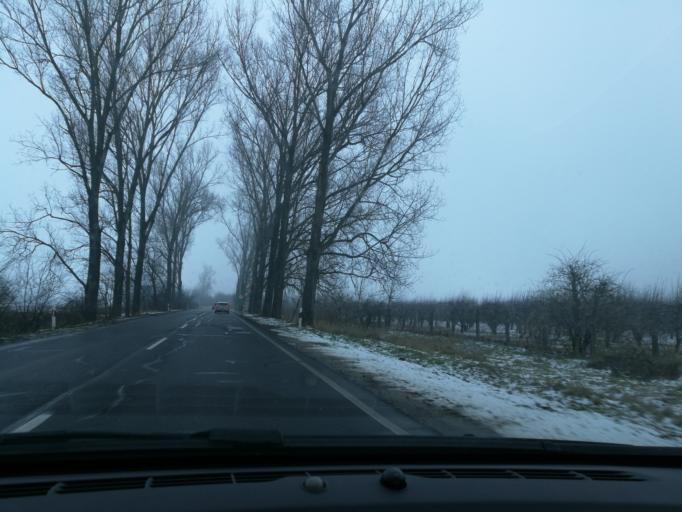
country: HU
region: Szabolcs-Szatmar-Bereg
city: Nyirpazony
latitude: 48.0186
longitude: 21.8402
